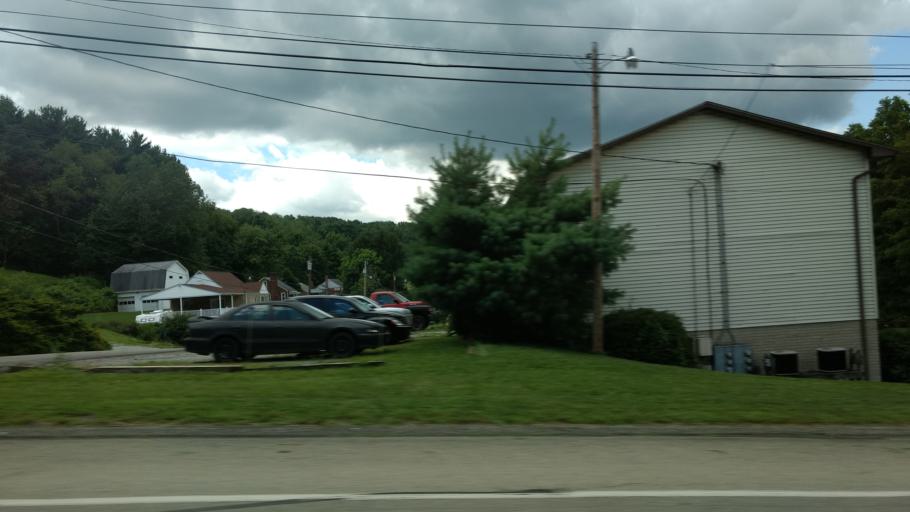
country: US
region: Pennsylvania
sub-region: Armstrong County
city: Apollo
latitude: 40.5625
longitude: -79.5799
